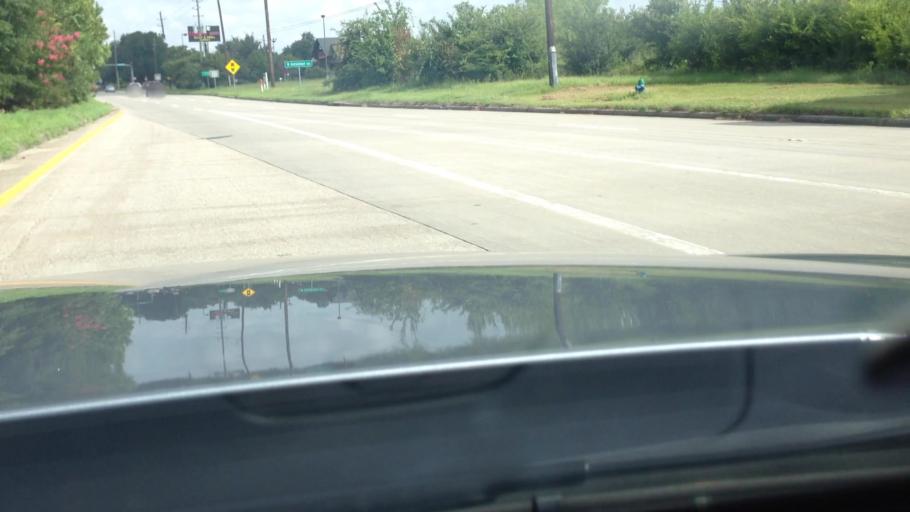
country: US
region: Texas
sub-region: Harris County
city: Hudson
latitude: 29.9521
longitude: -95.5355
